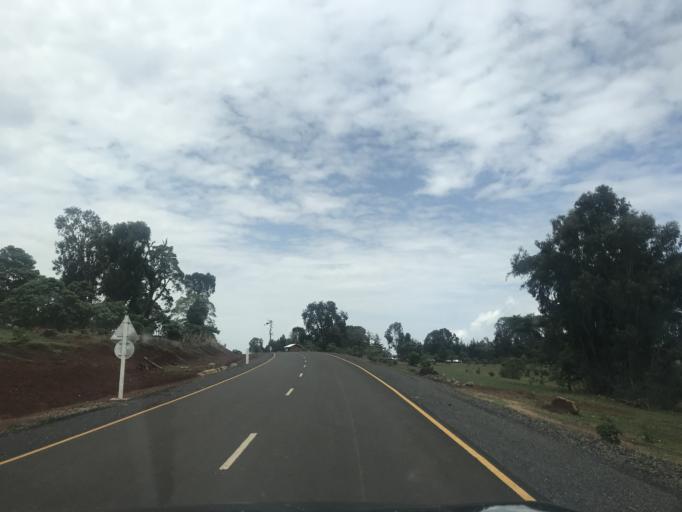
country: ET
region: Oromiya
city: Shambu
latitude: 9.8810
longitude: 36.6706
